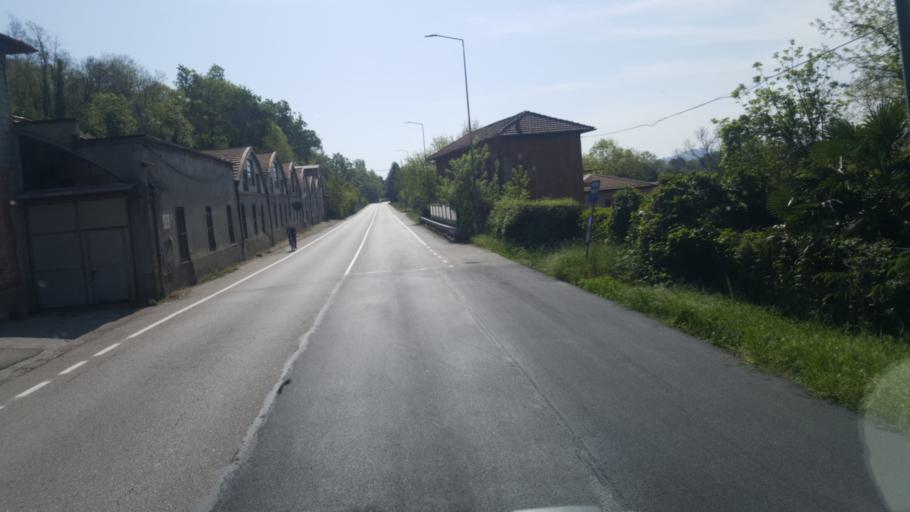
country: IT
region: Lombardy
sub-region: Provincia di Varese
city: Barasso
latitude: 45.8201
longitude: 8.7538
